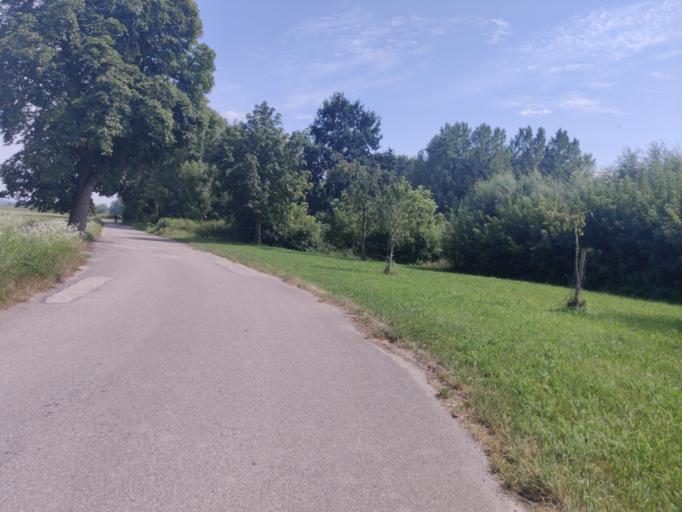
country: AT
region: Lower Austria
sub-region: Politischer Bezirk Amstetten
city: Zeillern
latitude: 48.1922
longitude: 14.7504
